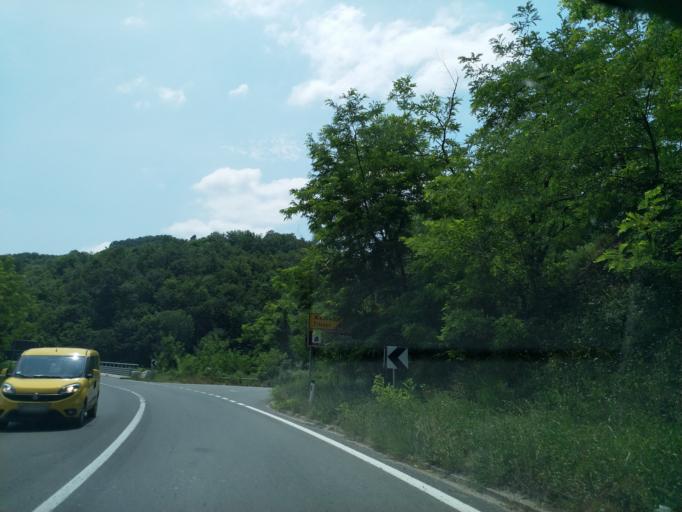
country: RS
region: Central Serbia
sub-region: Rasinski Okrug
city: Aleksandrovac
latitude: 43.4019
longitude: 21.1559
